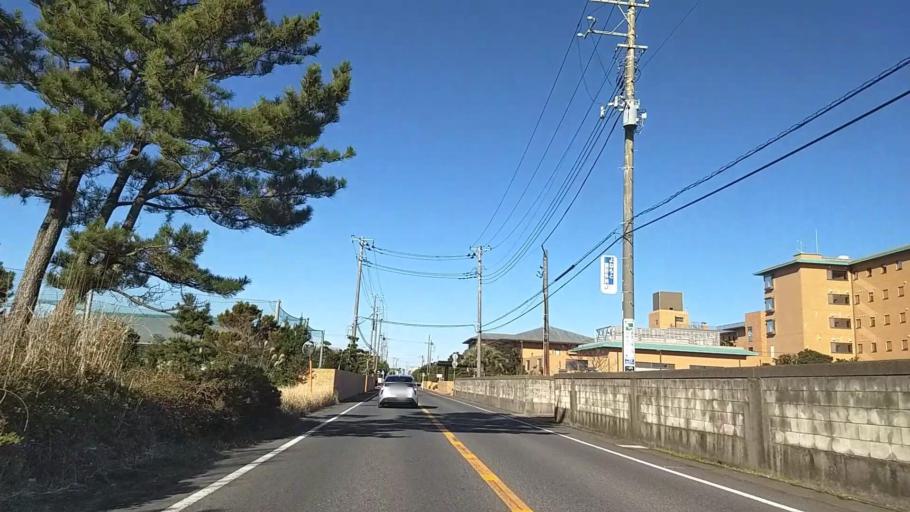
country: JP
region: Chiba
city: Mobara
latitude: 35.3741
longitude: 140.3876
